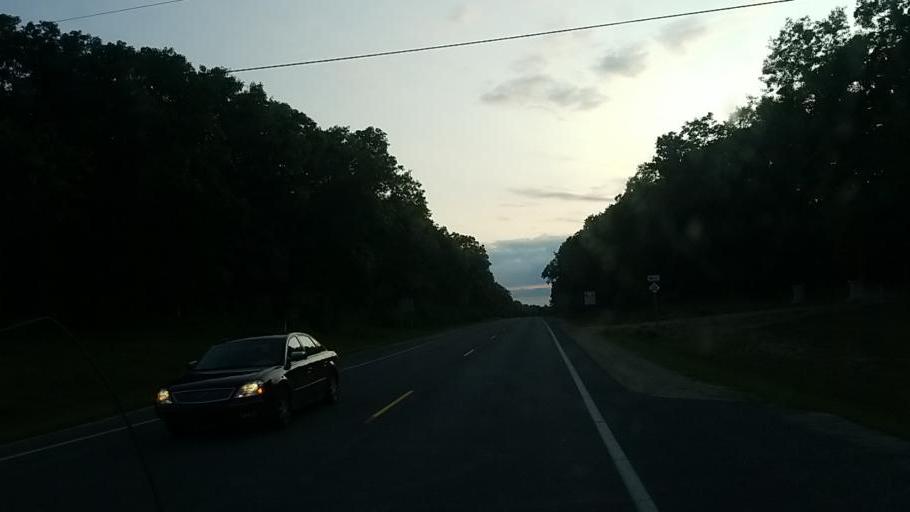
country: US
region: Michigan
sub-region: Newaygo County
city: Newaygo
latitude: 43.4051
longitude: -85.7224
